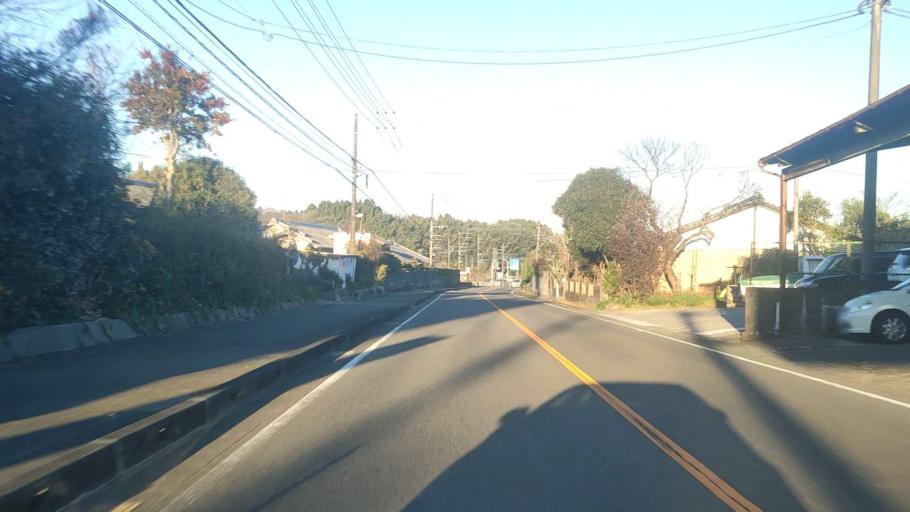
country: JP
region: Miyazaki
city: Miyazaki-shi
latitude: 31.8566
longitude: 131.3654
